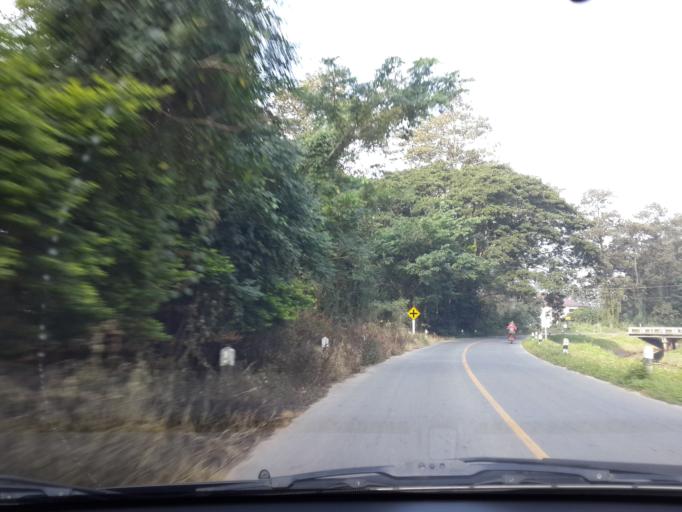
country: TH
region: Chiang Mai
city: San Sai
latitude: 18.8927
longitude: 99.0285
